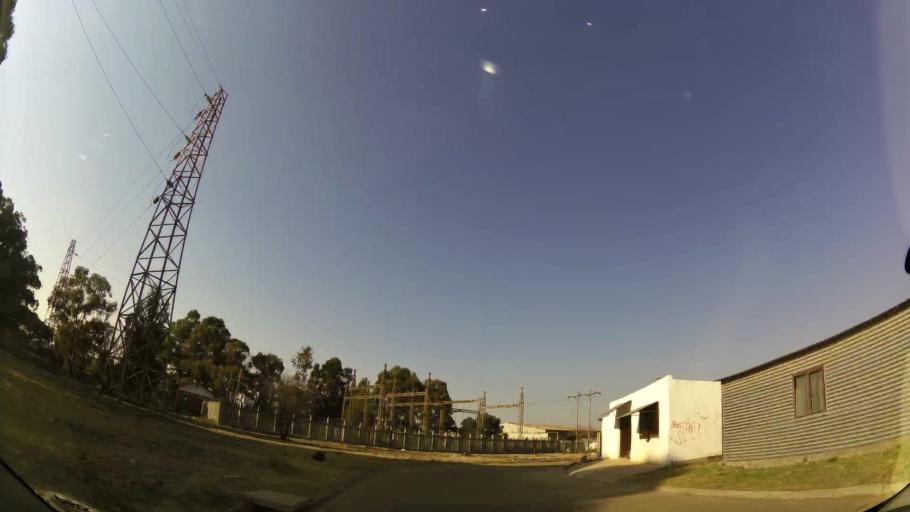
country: ZA
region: Gauteng
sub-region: Ekurhuleni Metropolitan Municipality
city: Boksburg
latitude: -26.1569
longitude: 28.2078
